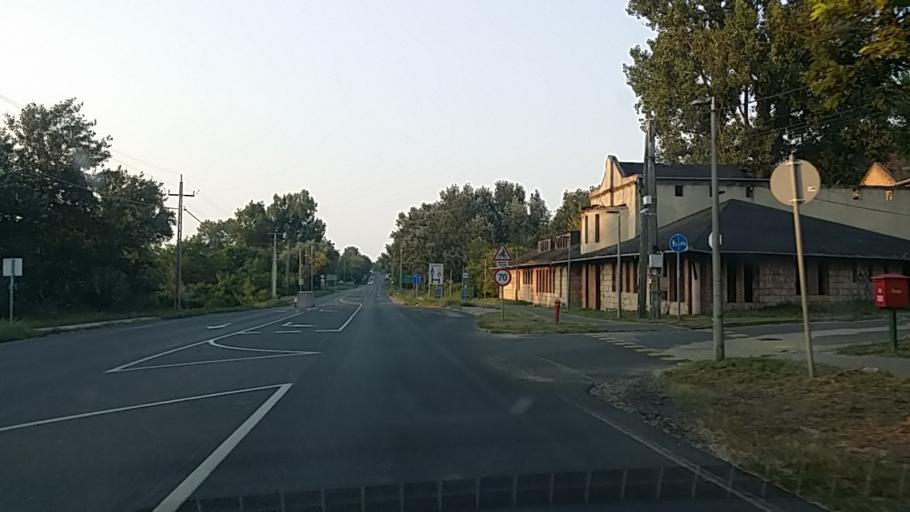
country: HU
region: Tolna
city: Dunafoldvar
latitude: 46.8289
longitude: 18.9077
